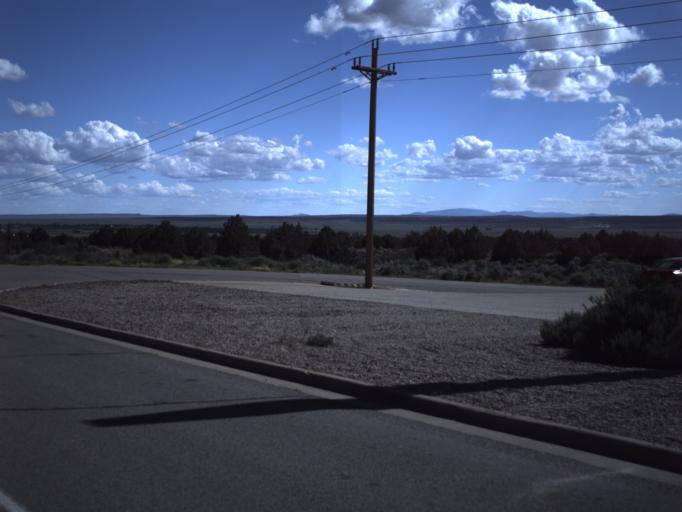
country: US
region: Arizona
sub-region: Mohave County
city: Colorado City
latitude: 37.0008
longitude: -112.9994
